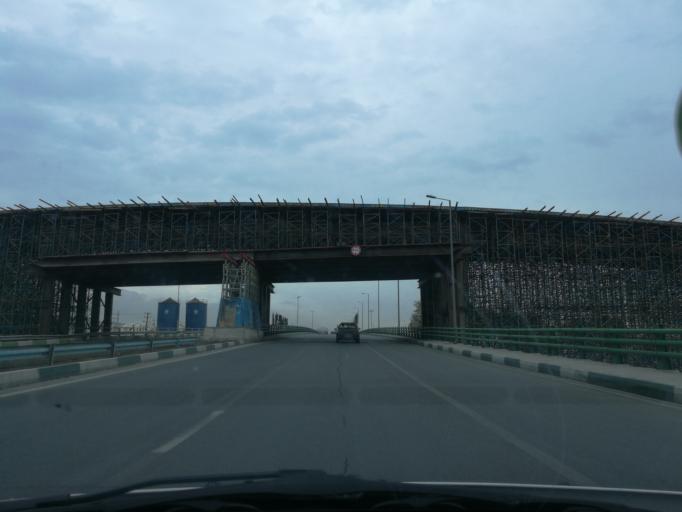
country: IR
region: Alborz
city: Karaj
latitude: 35.8505
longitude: 50.9071
